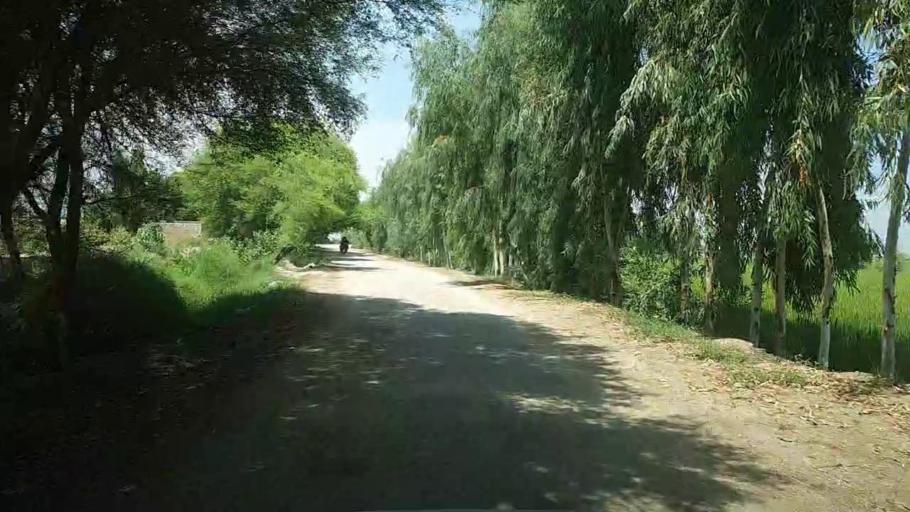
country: PK
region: Sindh
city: Kandhkot
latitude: 28.2998
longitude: 69.2359
